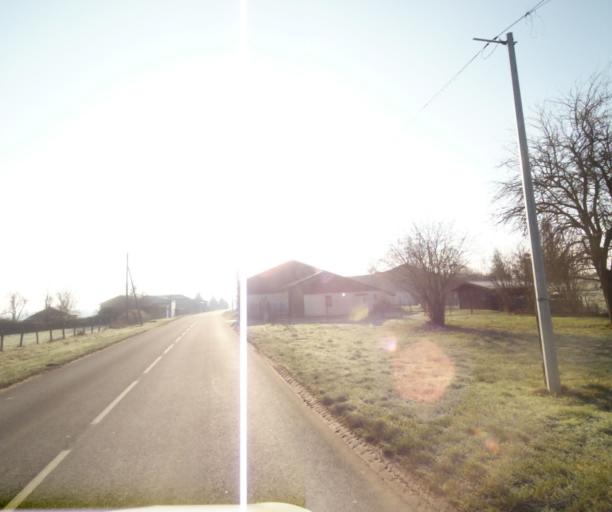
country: FR
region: Champagne-Ardenne
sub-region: Departement de la Haute-Marne
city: Montier-en-Der
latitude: 48.4607
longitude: 4.7674
